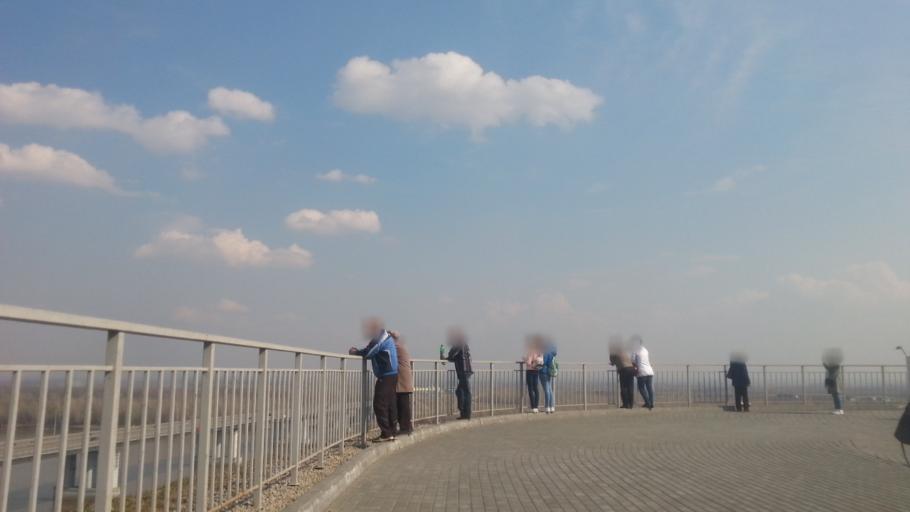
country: RU
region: Altai Krai
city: Zaton
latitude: 53.3238
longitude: 83.7964
